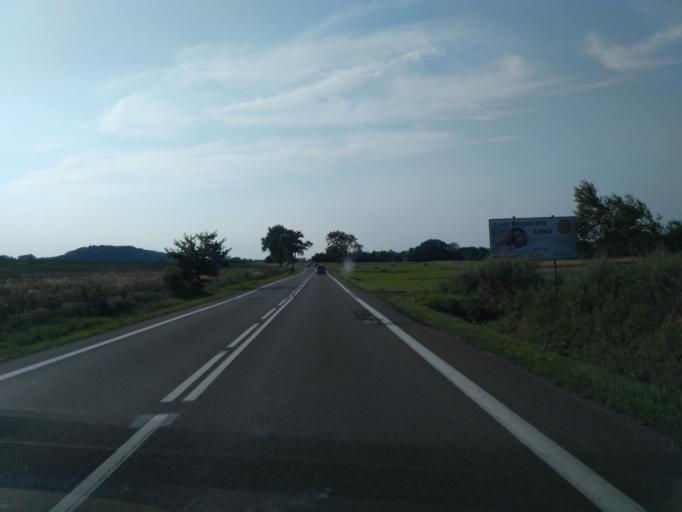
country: PL
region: Subcarpathian Voivodeship
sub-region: Powiat sanocki
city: Strachocina
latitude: 49.6060
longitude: 22.1289
